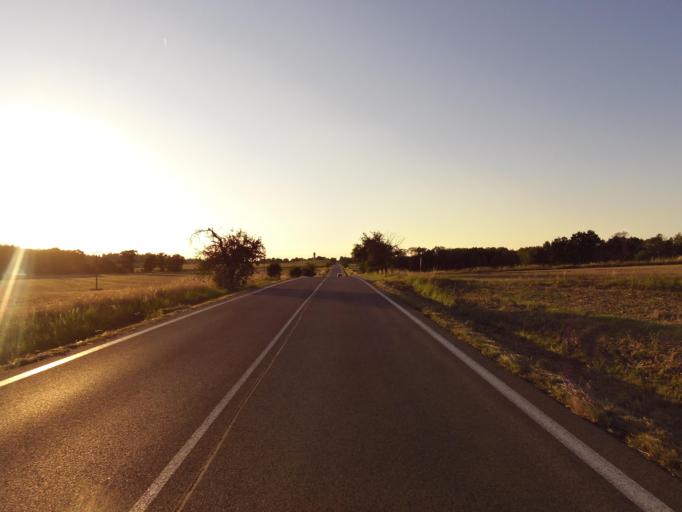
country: CZ
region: Central Bohemia
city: Mnichovo Hradiste
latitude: 50.5248
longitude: 14.9377
